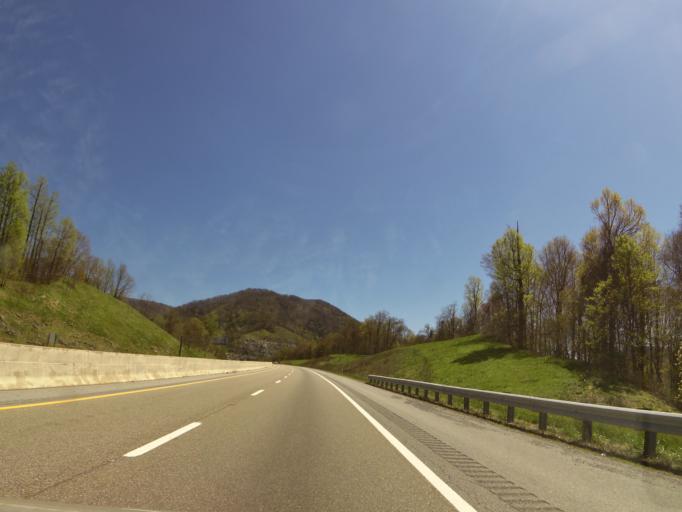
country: US
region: North Carolina
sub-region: Madison County
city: Mars Hill
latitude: 35.9937
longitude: -82.5443
